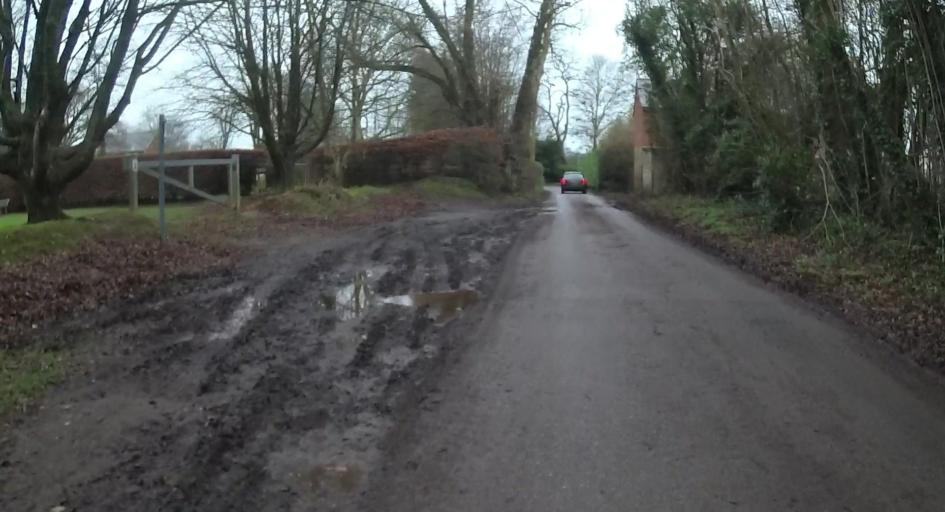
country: GB
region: England
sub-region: Hampshire
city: Four Marks
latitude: 51.1035
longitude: -1.0542
